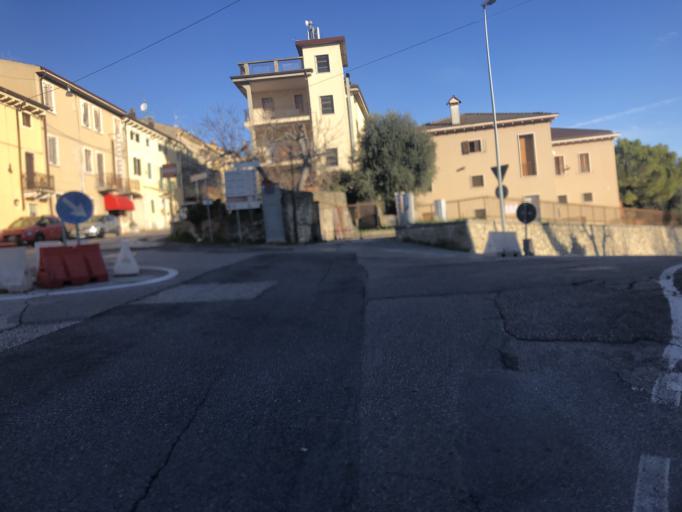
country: IT
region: Veneto
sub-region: Provincia di Verona
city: San Pietro in Cariano
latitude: 45.5164
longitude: 10.8862
